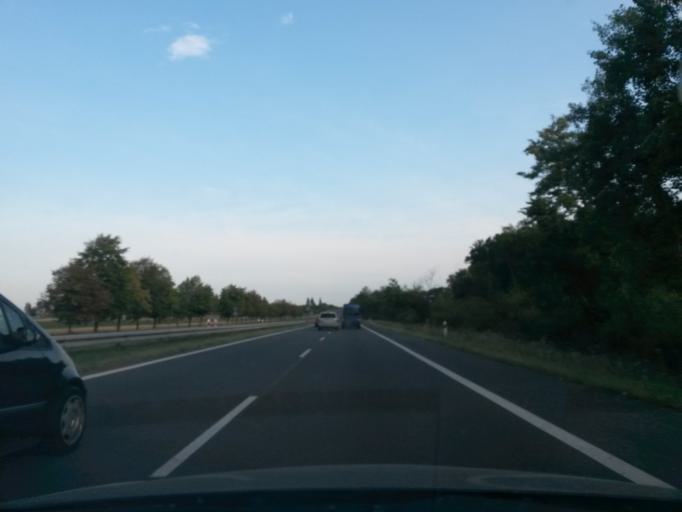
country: PL
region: Masovian Voivodeship
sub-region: Powiat plonski
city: Zaluski
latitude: 52.4967
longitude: 20.5415
